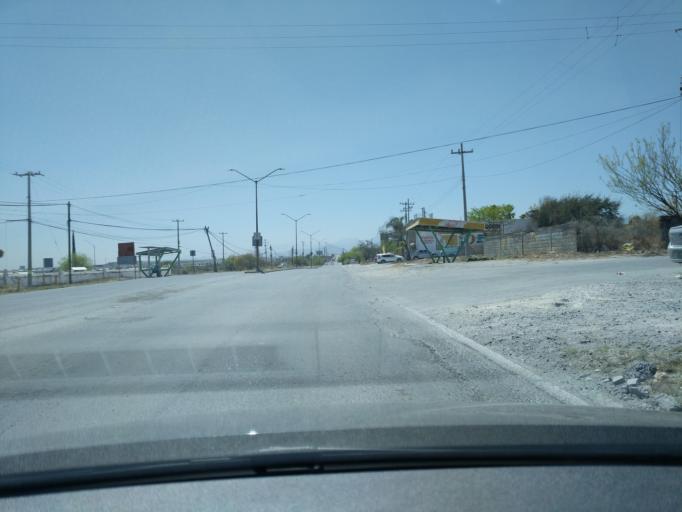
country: MX
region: Nuevo Leon
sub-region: Apodaca
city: Artemio Trevino
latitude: 25.8037
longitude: -100.1561
